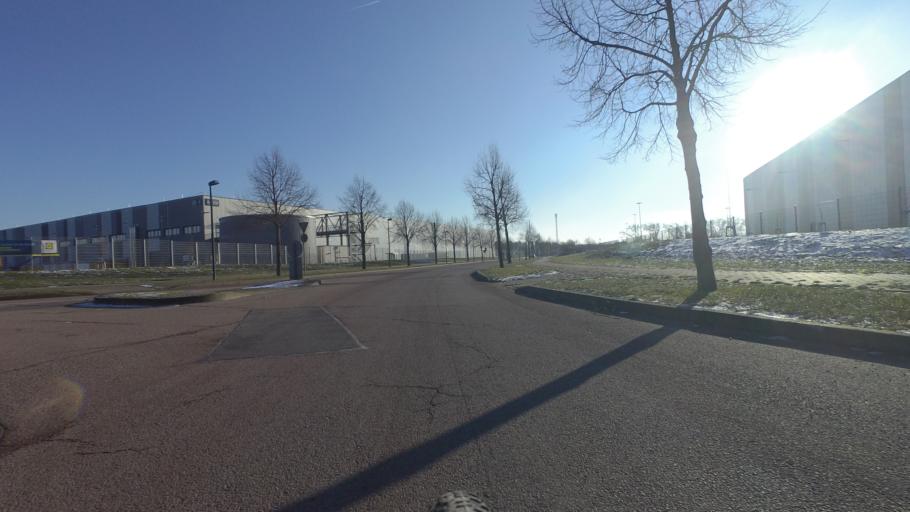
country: DE
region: Brandenburg
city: Ludwigsfelde
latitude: 52.3164
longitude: 13.2920
